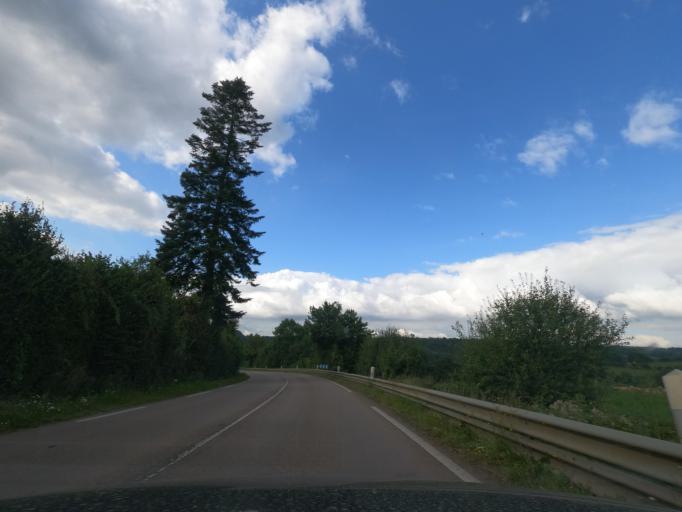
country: FR
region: Lower Normandy
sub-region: Departement de l'Orne
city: Gace
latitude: 48.8047
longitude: 0.3107
